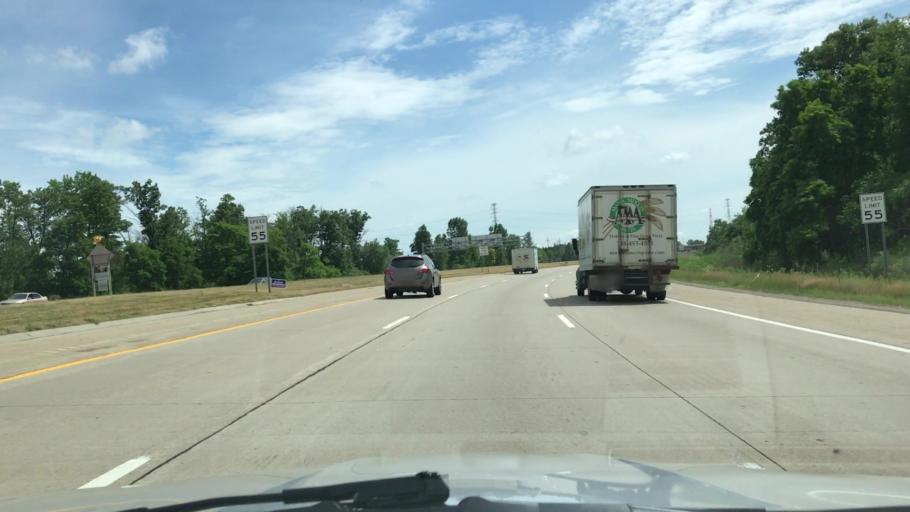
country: US
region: Michigan
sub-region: Oakland County
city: Wolverine Lake
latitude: 42.5520
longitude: -83.4481
